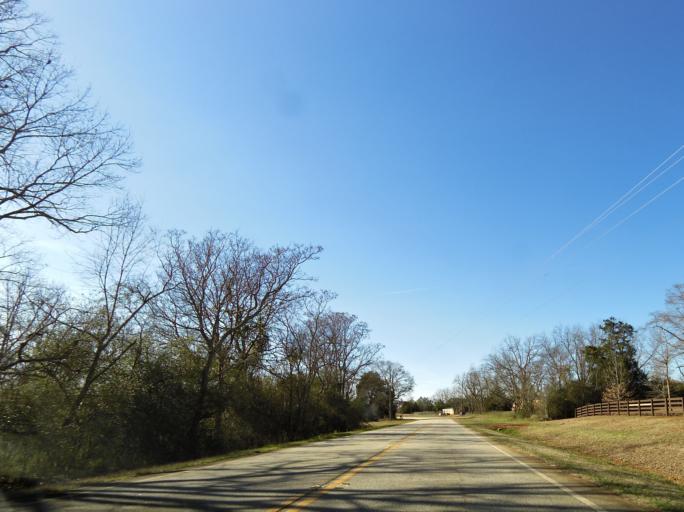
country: US
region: Georgia
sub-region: Crawford County
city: Roberta
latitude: 32.8770
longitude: -84.0753
